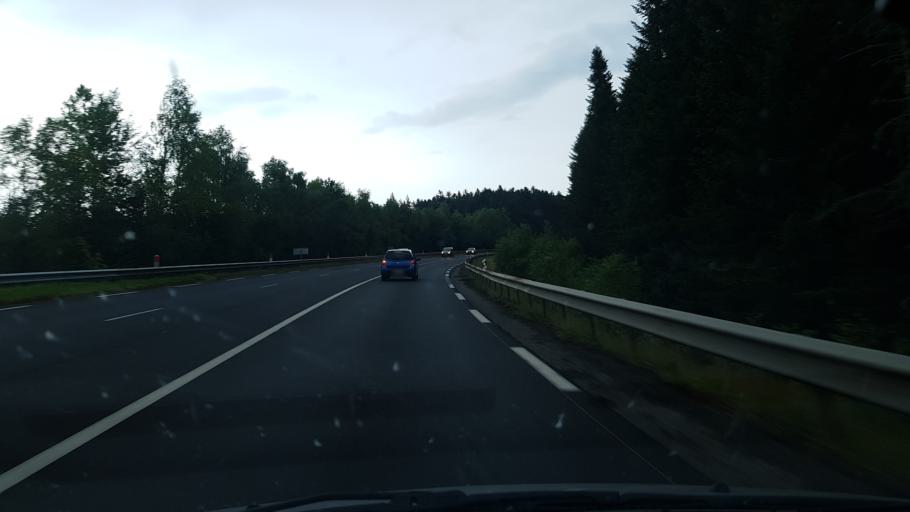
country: FR
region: Auvergne
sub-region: Departement de la Haute-Loire
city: Allegre
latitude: 45.1449
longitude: 3.6451
